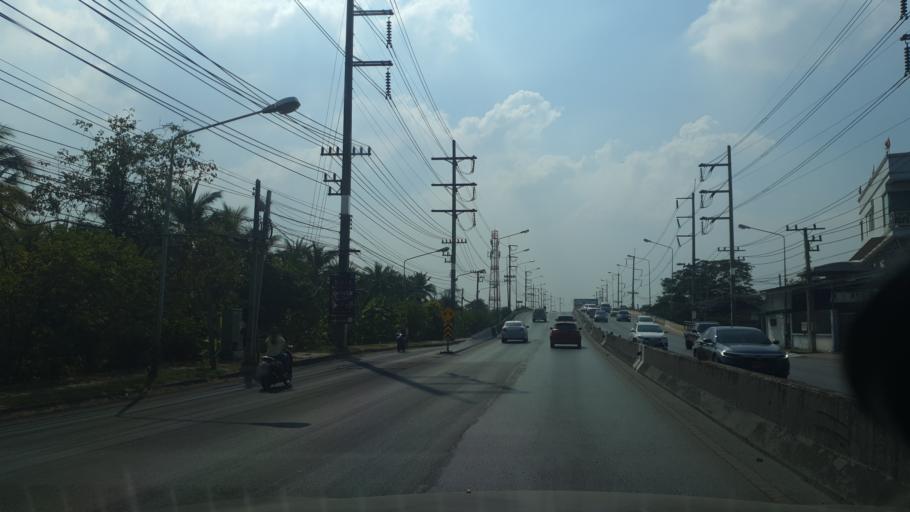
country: TH
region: Samut Sakhon
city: Krathum Baen
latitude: 13.6602
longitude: 100.2741
